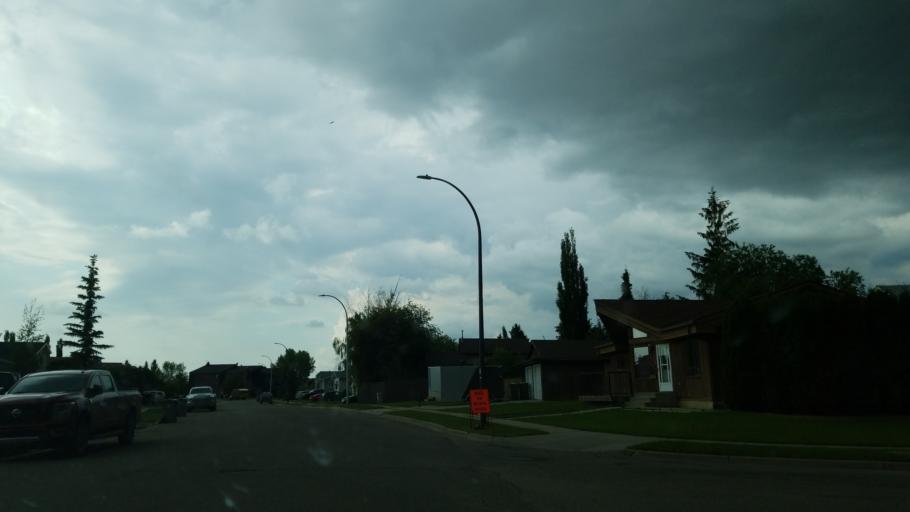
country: CA
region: Saskatchewan
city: Lloydminster
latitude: 53.2629
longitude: -110.0199
